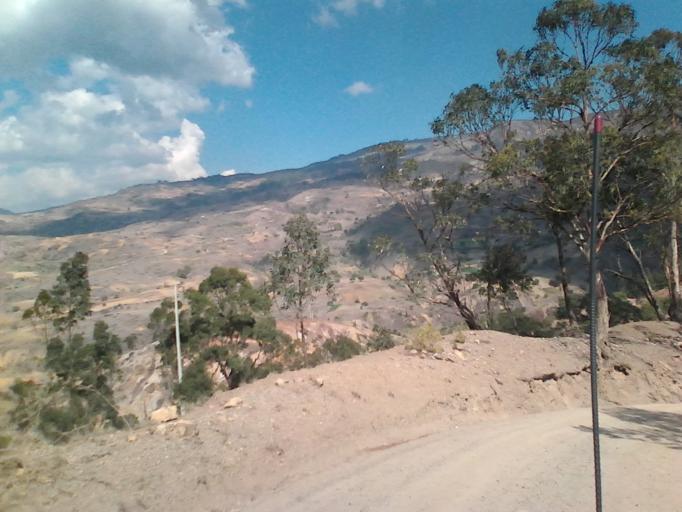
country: CO
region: Boyaca
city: Sachica
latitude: 5.5784
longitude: -73.5147
